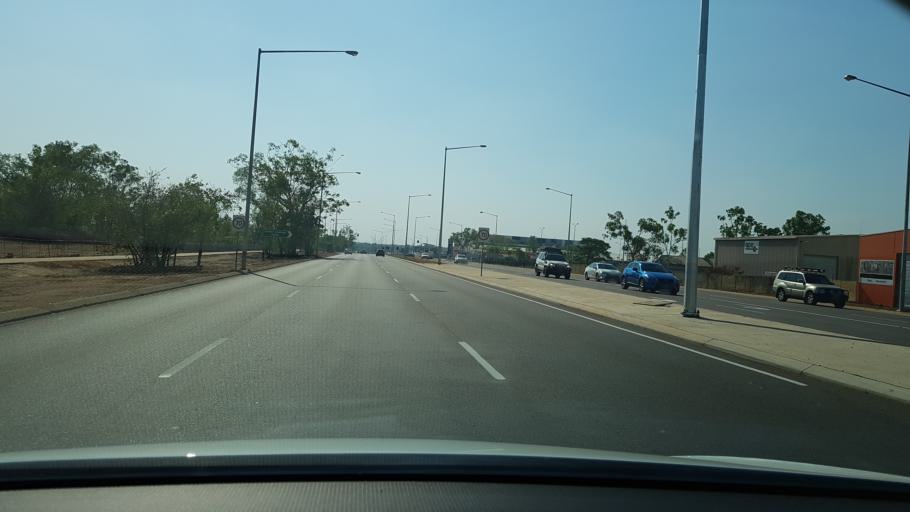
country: AU
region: Northern Territory
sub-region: Palmerston
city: Palmerston
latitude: -12.4757
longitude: 130.9851
